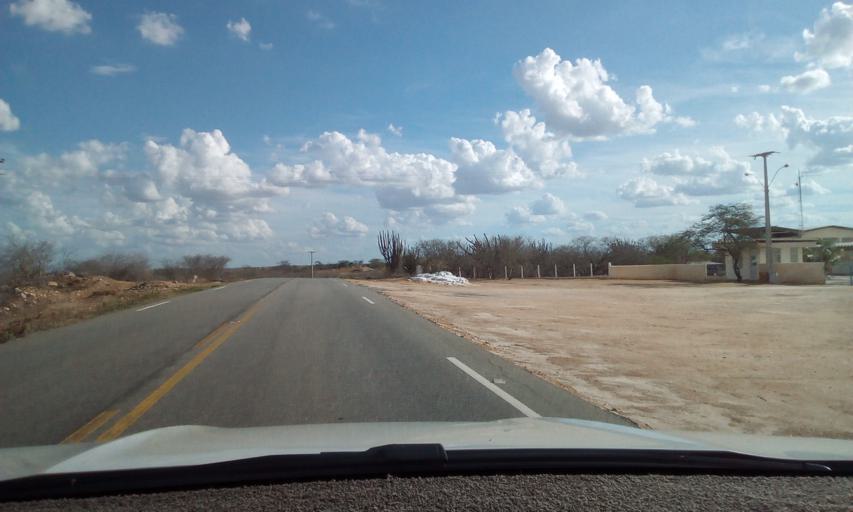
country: BR
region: Paraiba
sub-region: Soledade
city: Soledade
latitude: -6.8191
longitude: -36.4045
